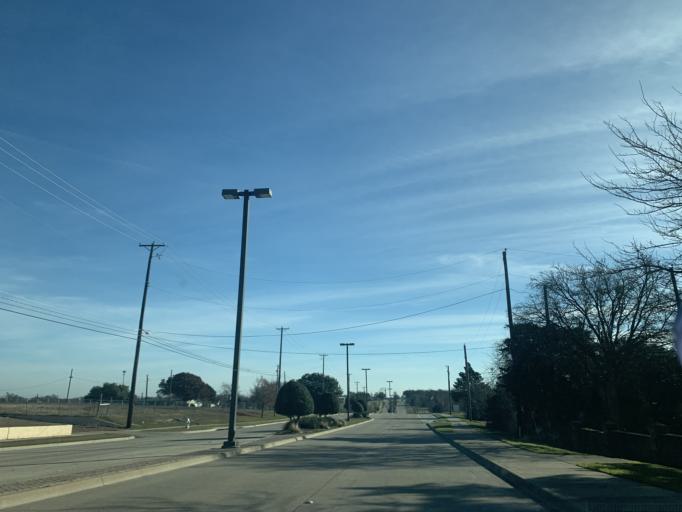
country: US
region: Texas
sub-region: Dallas County
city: DeSoto
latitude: 32.5751
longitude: -96.8343
